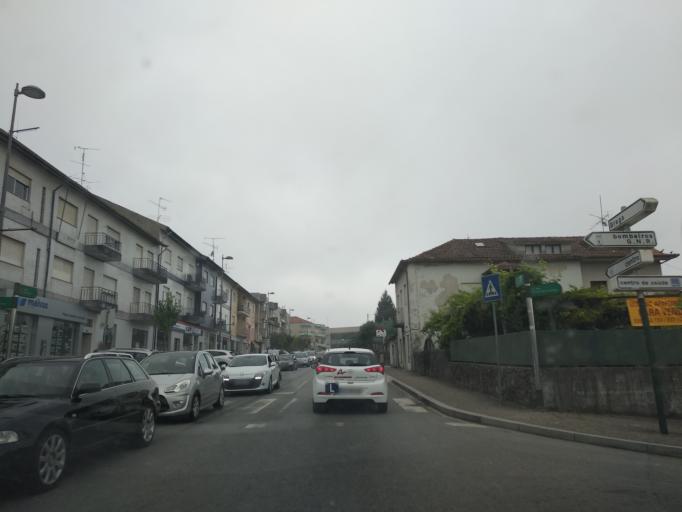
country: PT
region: Braga
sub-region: Vila Verde
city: Vila Verde
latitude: 41.6464
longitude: -8.4361
